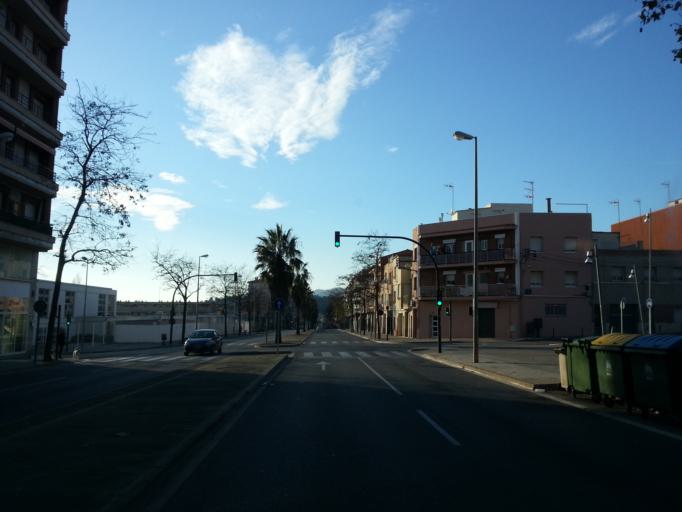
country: ES
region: Catalonia
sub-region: Provincia de Barcelona
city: Terrassa
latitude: 41.5800
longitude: 2.0123
